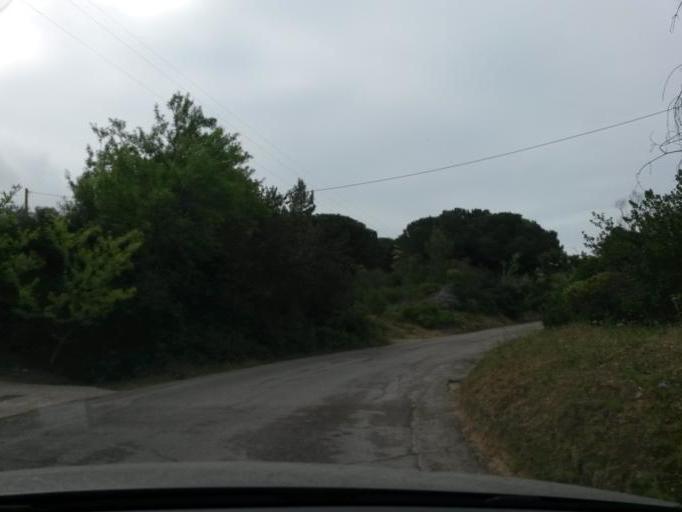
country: IT
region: Tuscany
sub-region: Provincia di Livorno
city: Capoliveri
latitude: 42.7393
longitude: 10.3718
